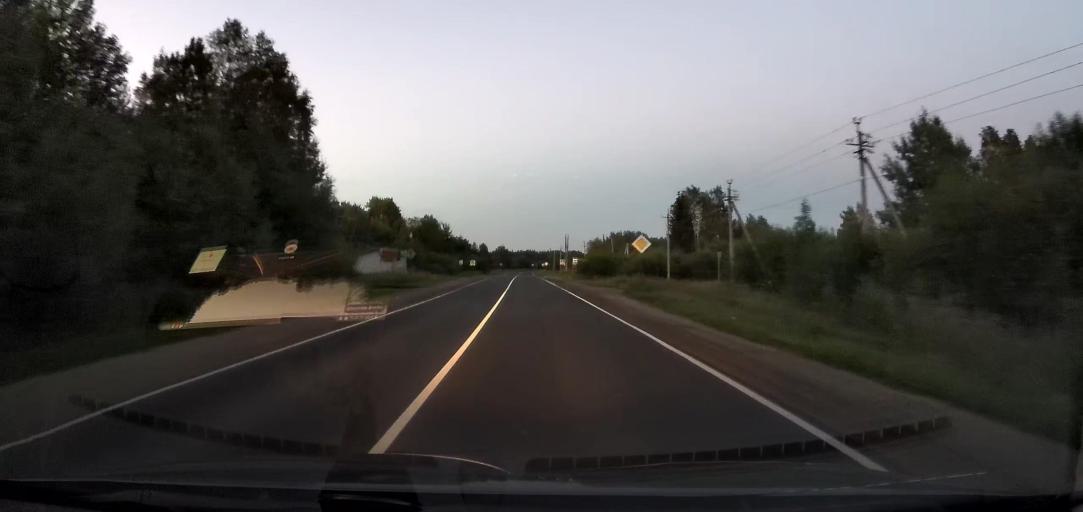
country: RU
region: Arkhangelskaya
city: Uyemskiy
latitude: 64.4416
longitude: 40.9564
